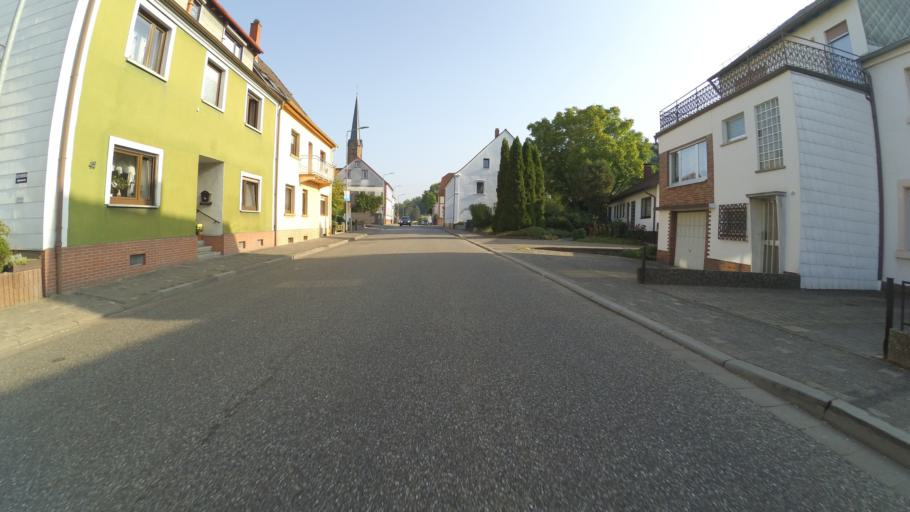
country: DE
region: Rheinland-Pfalz
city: Hauptstuhl
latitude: 49.3884
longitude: 7.4636
